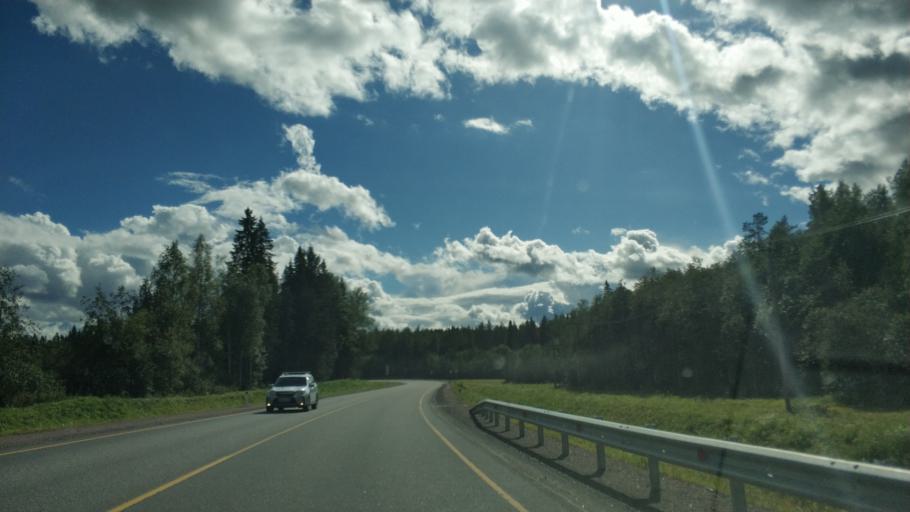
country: RU
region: Republic of Karelia
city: Ruskeala
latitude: 61.9143
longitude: 30.6266
